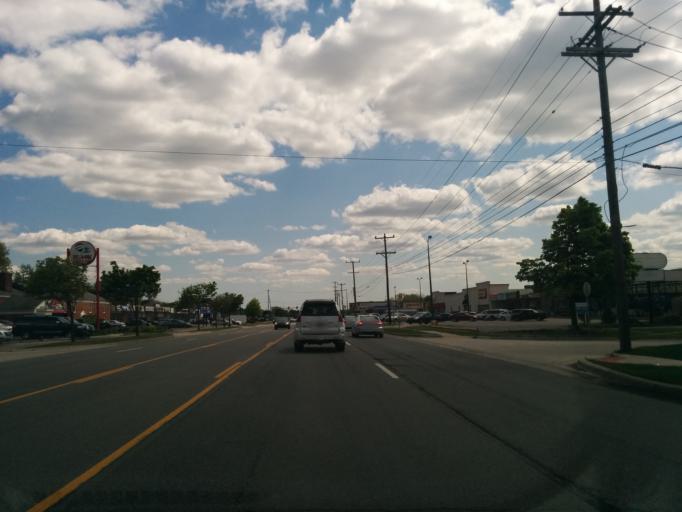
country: US
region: Michigan
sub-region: Oakland County
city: Farmington Hills
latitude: 42.5165
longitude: -83.3595
